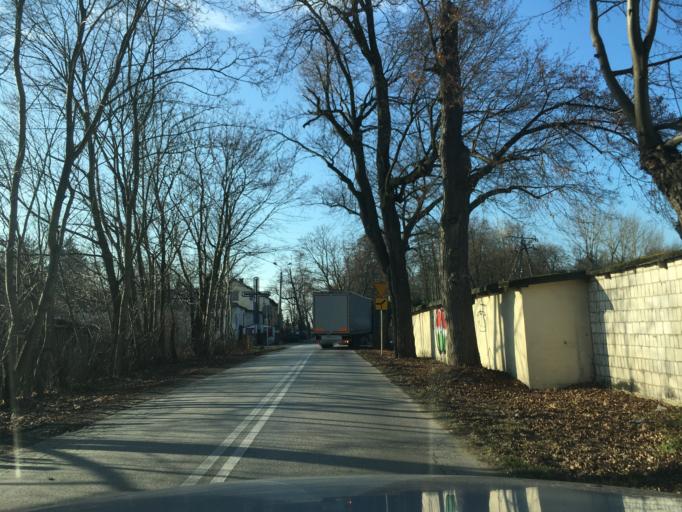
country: PL
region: Masovian Voivodeship
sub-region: Powiat pruszkowski
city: Nadarzyn
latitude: 52.0477
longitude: 20.7864
